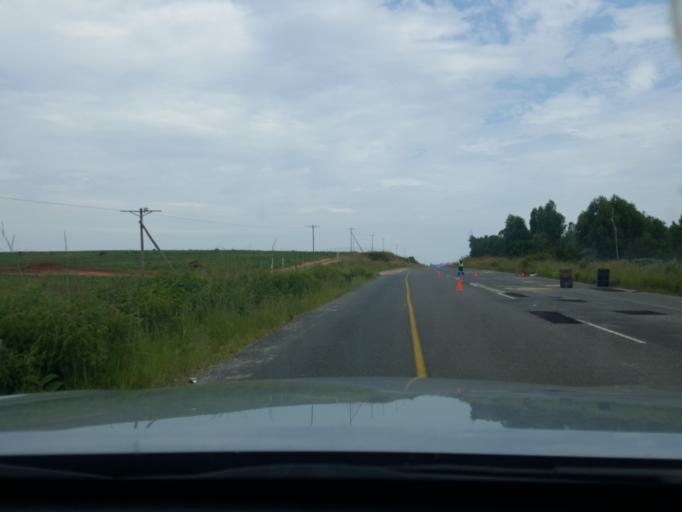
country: ZA
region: Mpumalanga
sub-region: Ehlanzeni District
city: White River
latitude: -25.3013
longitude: 30.9823
